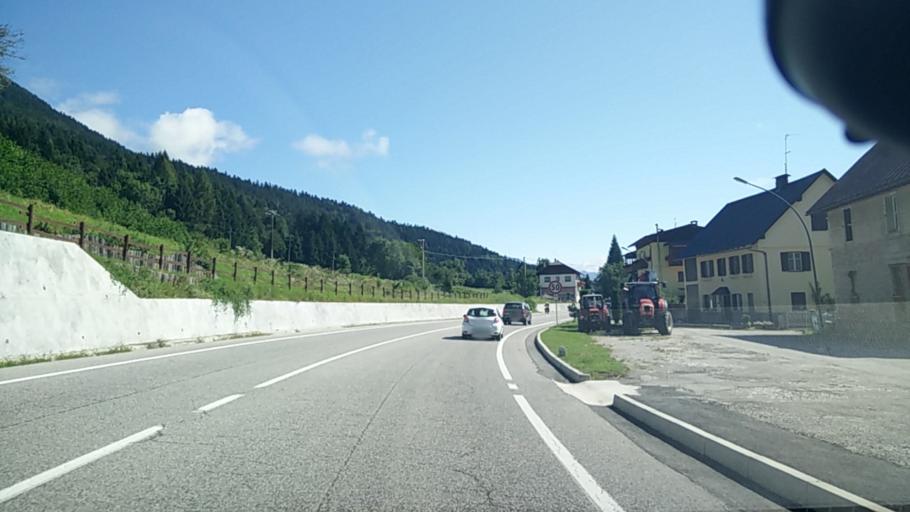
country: IT
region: Friuli Venezia Giulia
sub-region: Provincia di Udine
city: Tarvisio
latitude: 46.5224
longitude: 13.6172
